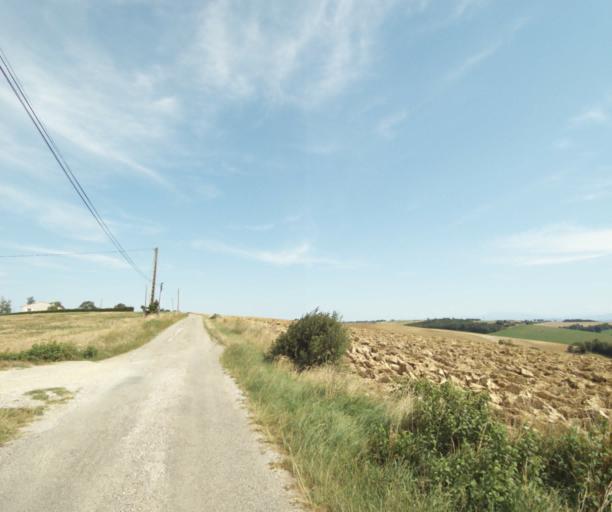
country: FR
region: Midi-Pyrenees
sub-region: Departement de l'Ariege
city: Lezat-sur-Leze
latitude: 43.2647
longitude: 1.4037
